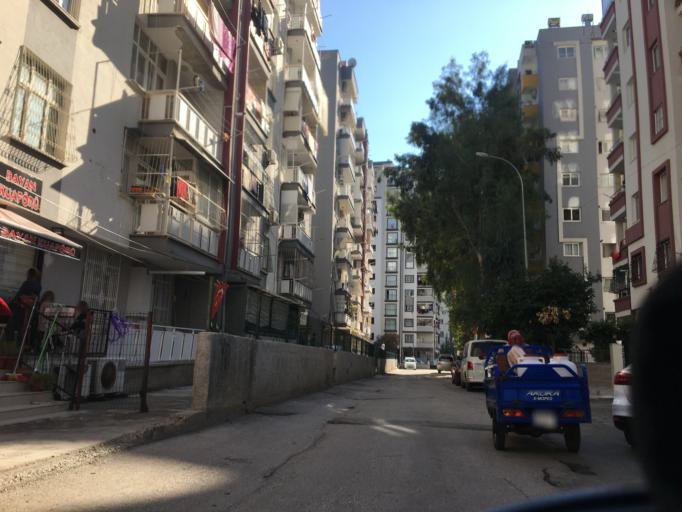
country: TR
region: Adana
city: Seyhan
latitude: 37.0232
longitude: 35.2862
